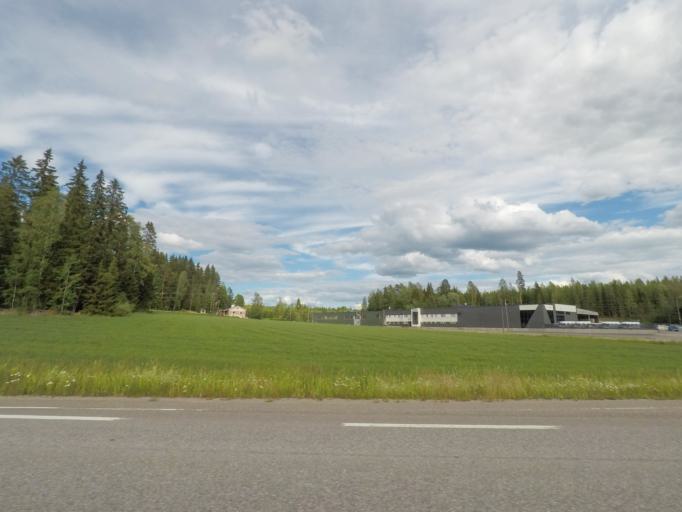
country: FI
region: Paijanne Tavastia
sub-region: Lahti
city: Hollola
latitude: 60.8653
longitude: 25.5013
